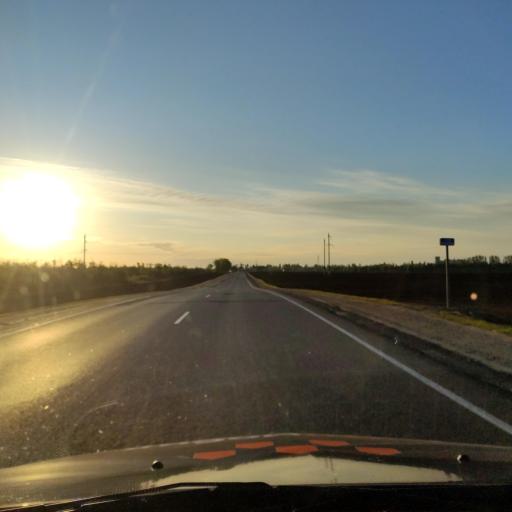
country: RU
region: Orjol
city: Livny
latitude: 52.4410
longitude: 37.5612
